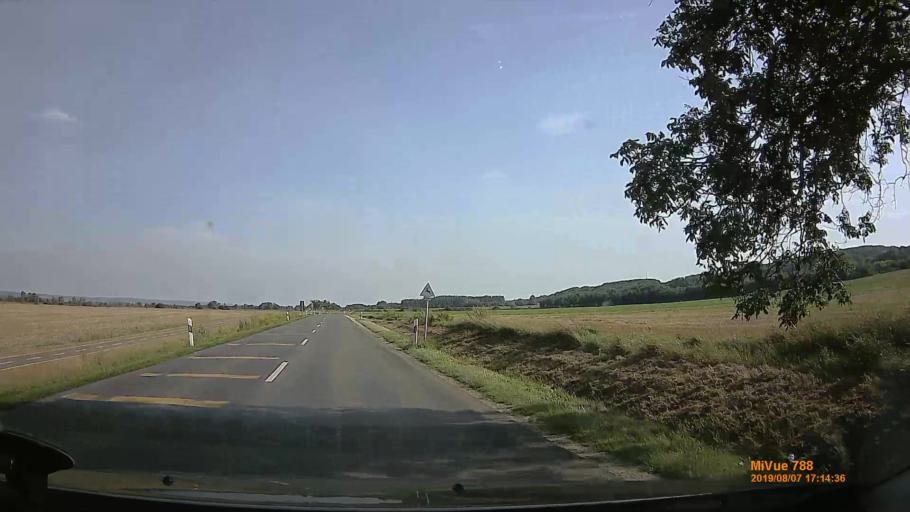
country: HU
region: Zala
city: Pacsa
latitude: 46.6688
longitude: 16.9164
